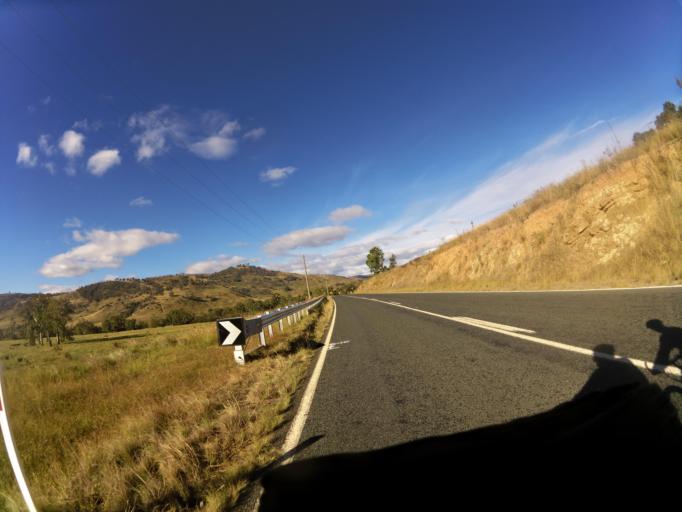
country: AU
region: New South Wales
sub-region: Greater Hume Shire
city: Holbrook
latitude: -35.9655
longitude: 147.7623
